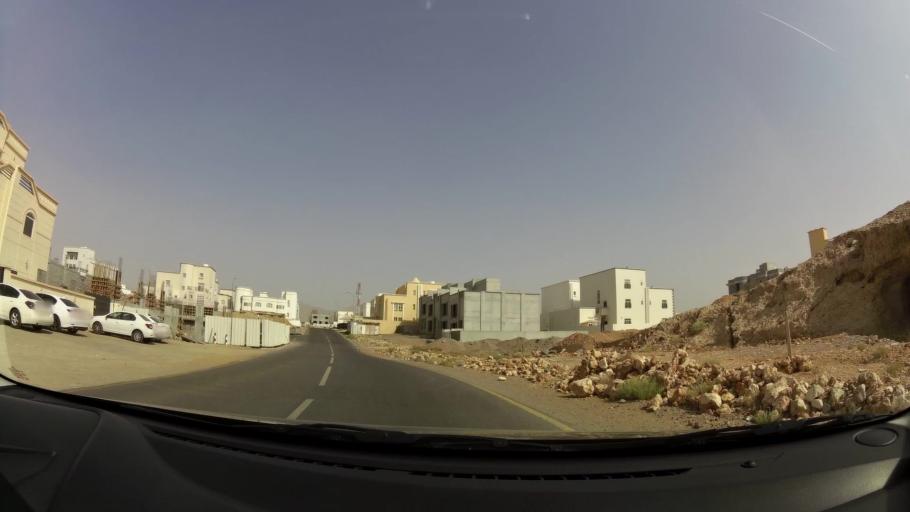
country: OM
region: Muhafazat Masqat
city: Bawshar
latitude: 23.5554
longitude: 58.3490
